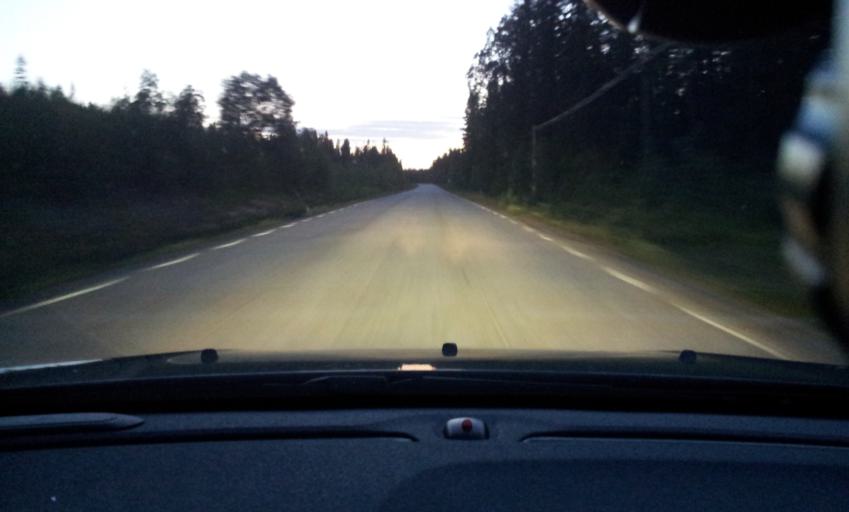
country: SE
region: Jaemtland
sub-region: Bergs Kommun
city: Hoverberg
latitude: 62.7445
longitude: 14.5809
